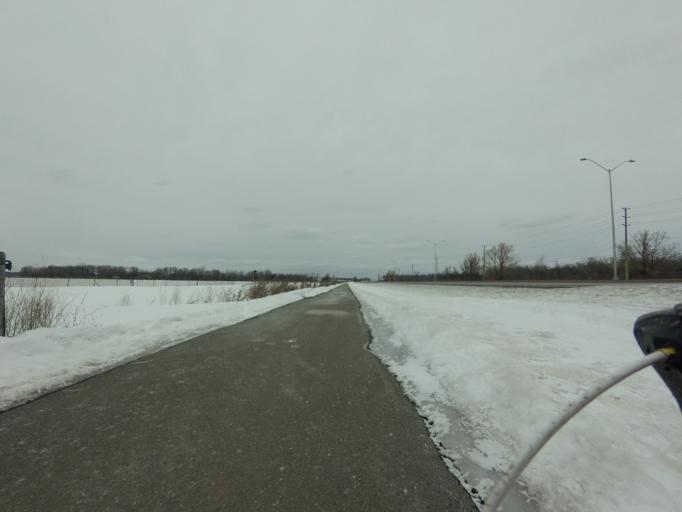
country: CA
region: Ontario
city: Ottawa
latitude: 45.3105
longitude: -75.6843
